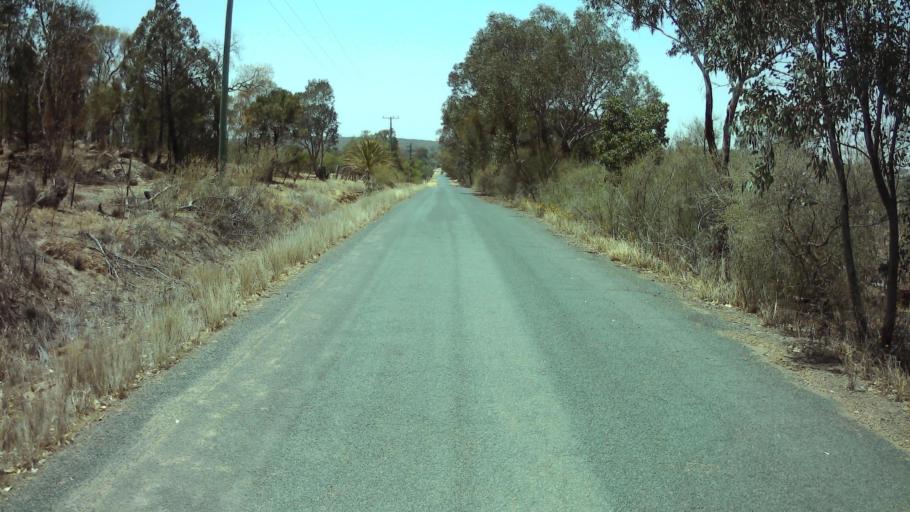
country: AU
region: New South Wales
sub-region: Weddin
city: Grenfell
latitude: -33.8885
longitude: 148.1465
